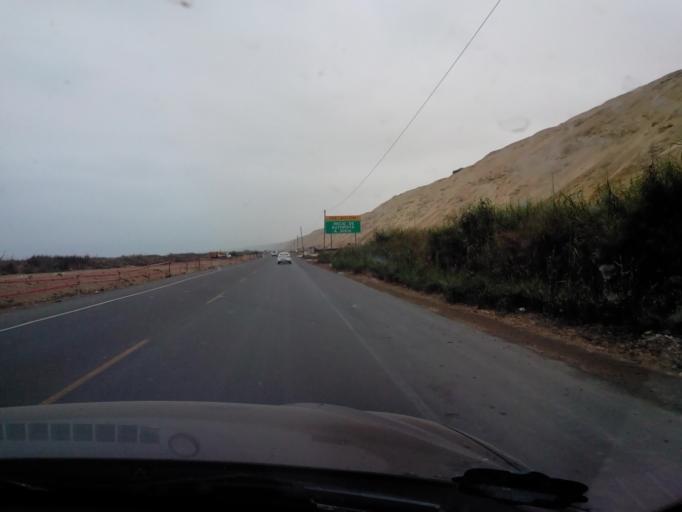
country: PE
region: Ica
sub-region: Provincia de Chincha
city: San Pedro
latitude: -13.4062
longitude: -76.1924
